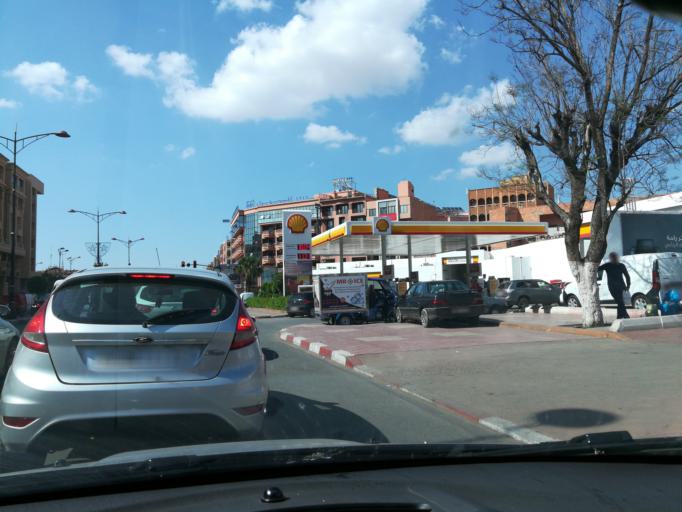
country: MA
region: Marrakech-Tensift-Al Haouz
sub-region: Marrakech
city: Marrakesh
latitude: 31.6368
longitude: -8.0175
